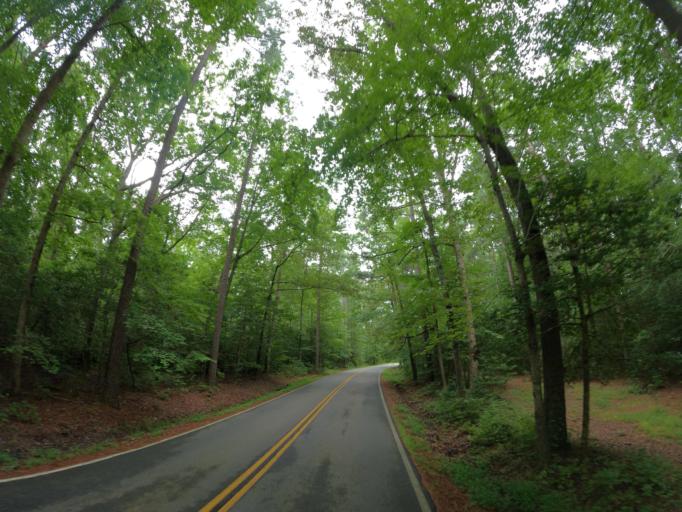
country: US
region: Maryland
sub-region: Saint Mary's County
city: California
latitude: 38.2409
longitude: -76.5434
